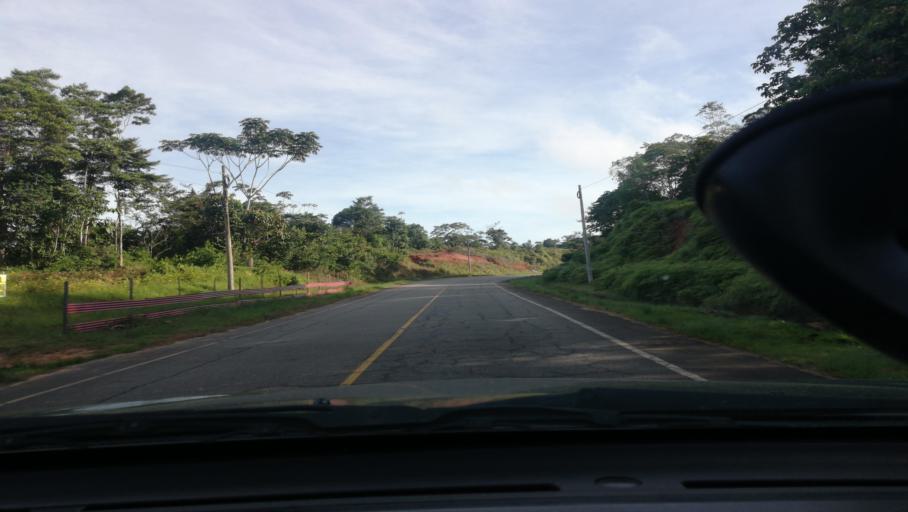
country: PE
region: Loreto
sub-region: Provincia de Loreto
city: Nauta
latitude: -4.4150
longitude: -73.5842
